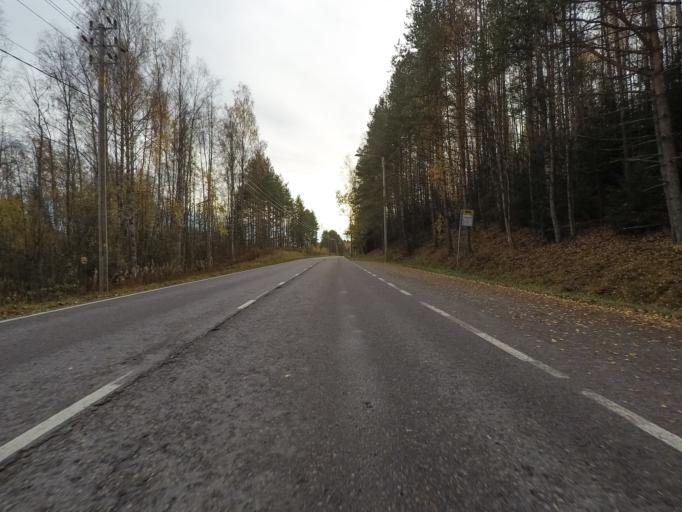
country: FI
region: Uusimaa
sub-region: Helsinki
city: Vantaa
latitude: 60.2645
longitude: 25.1403
